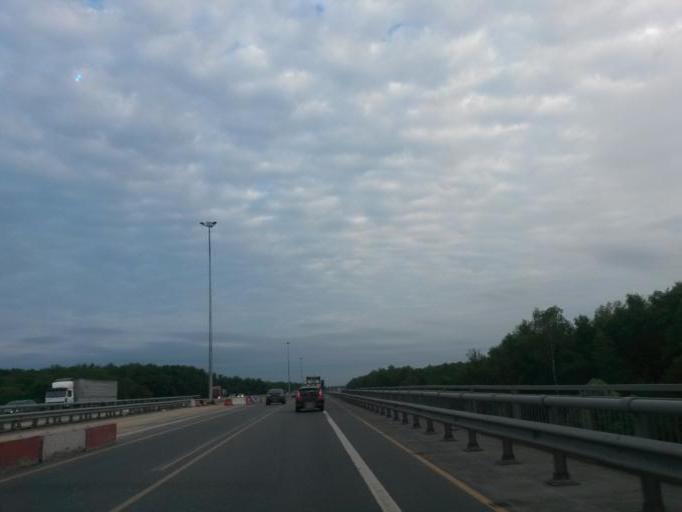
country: RU
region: Moskovskaya
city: Lyubuchany
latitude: 55.2090
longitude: 37.5351
